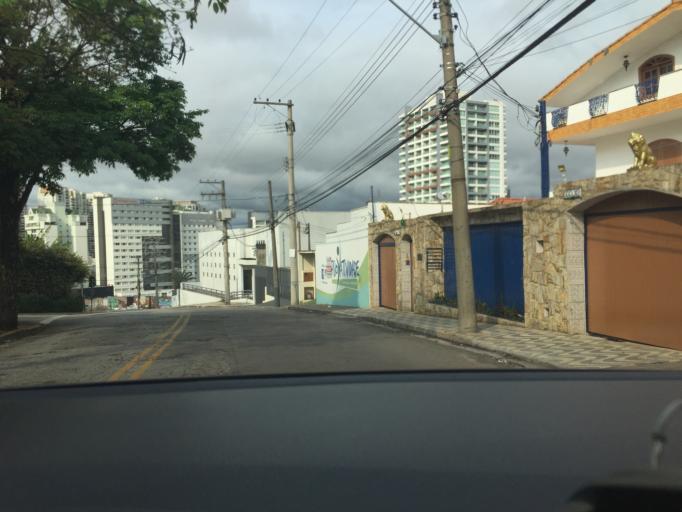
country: BR
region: Sao Paulo
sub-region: Jundiai
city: Jundiai
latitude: -23.2028
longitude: -46.8941
